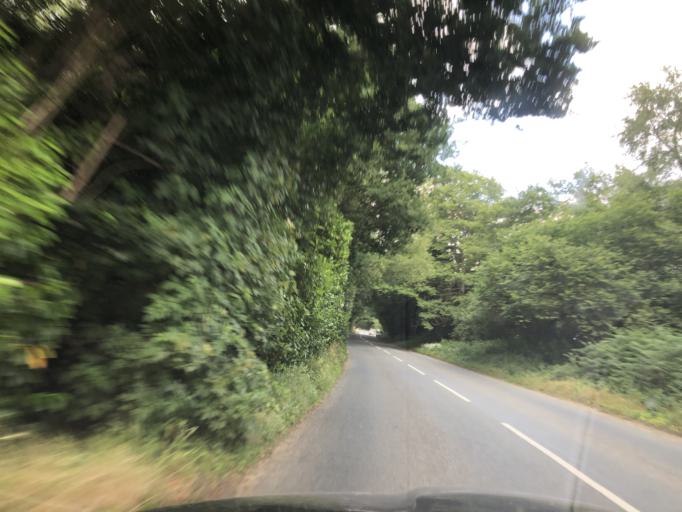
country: GB
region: England
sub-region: Hampshire
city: Eversley
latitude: 51.3464
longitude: -0.8910
